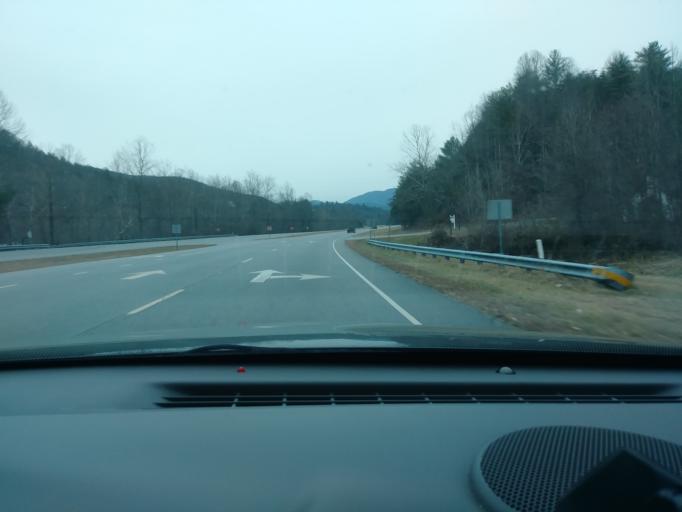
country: US
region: North Carolina
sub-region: Wilkes County
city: Millers Creek
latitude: 36.1817
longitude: -81.3972
